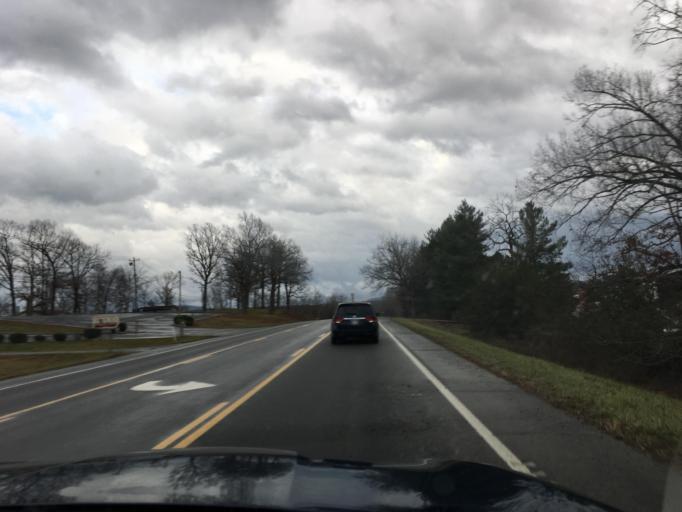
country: US
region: Tennessee
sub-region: Cumberland County
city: Crossville
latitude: 35.9221
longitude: -85.0005
